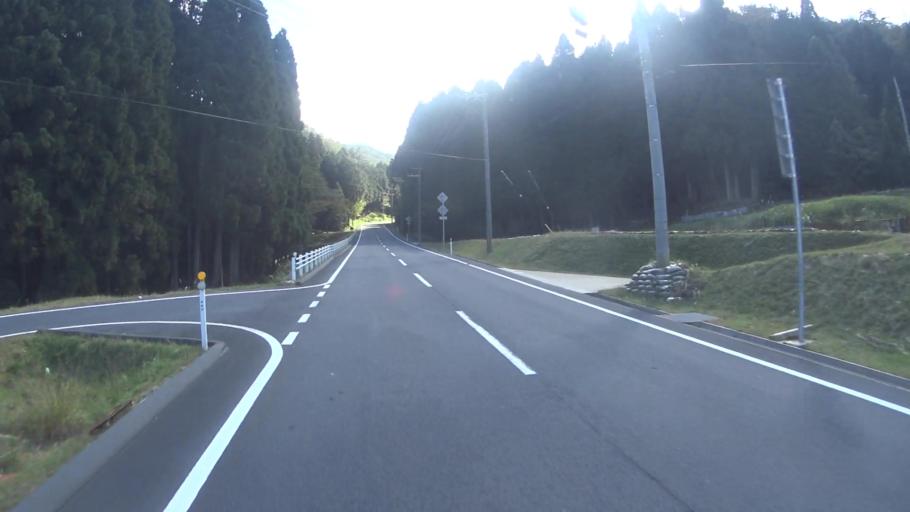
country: JP
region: Hyogo
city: Toyooka
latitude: 35.5407
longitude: 134.9773
